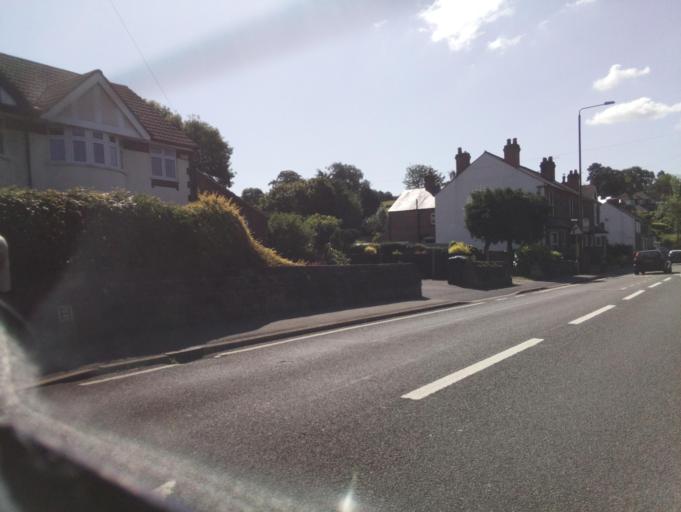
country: GB
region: England
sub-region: Derbyshire
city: Belper
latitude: 53.0100
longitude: -1.4810
